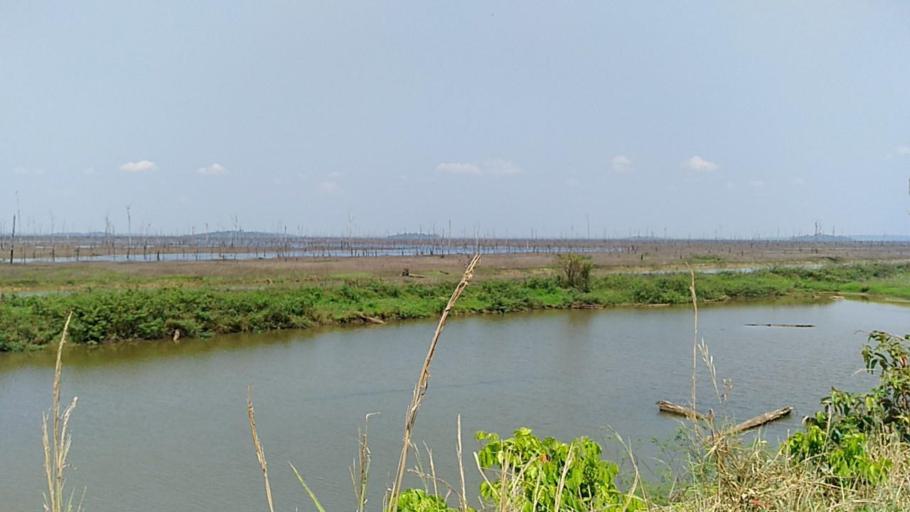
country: BR
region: Rondonia
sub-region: Porto Velho
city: Porto Velho
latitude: -8.7839
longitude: -63.3188
